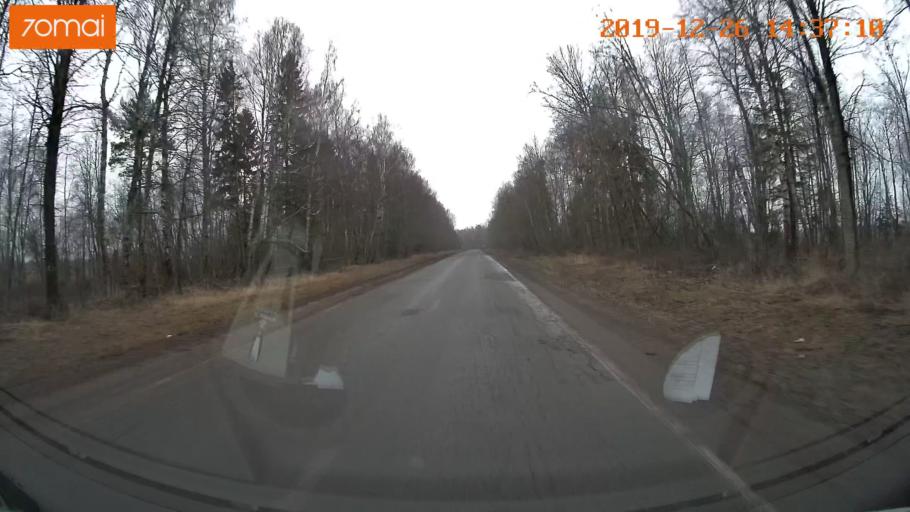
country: RU
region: Jaroslavl
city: Poshekhon'ye
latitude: 58.4046
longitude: 38.9733
